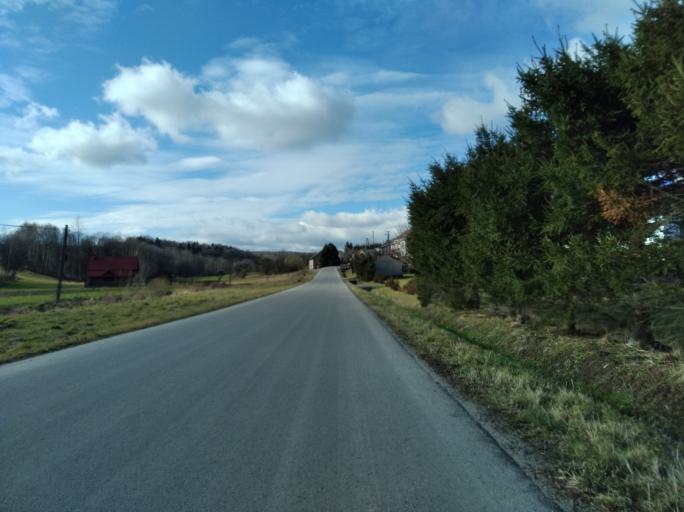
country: PL
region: Subcarpathian Voivodeship
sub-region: Powiat strzyzowski
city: Wisniowa
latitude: 49.9132
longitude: 21.6755
